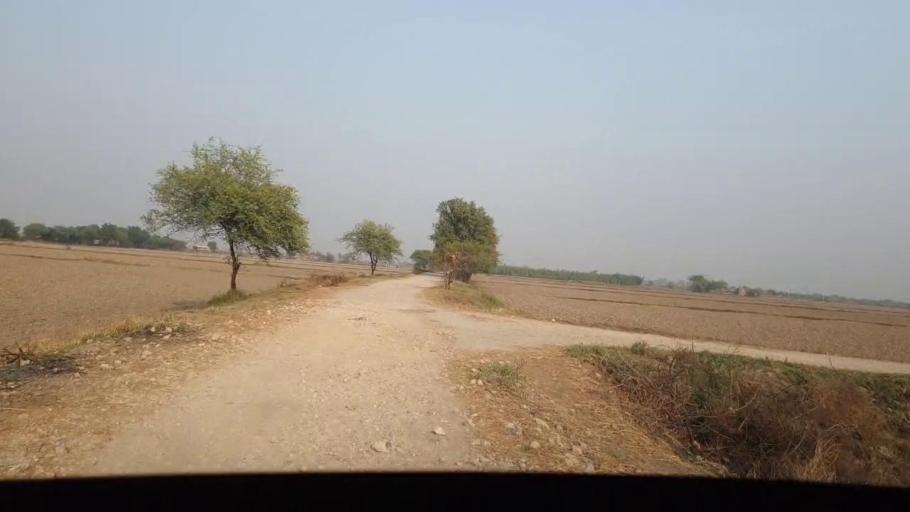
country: PK
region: Sindh
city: Chuhar Jamali
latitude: 24.2572
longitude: 68.1125
